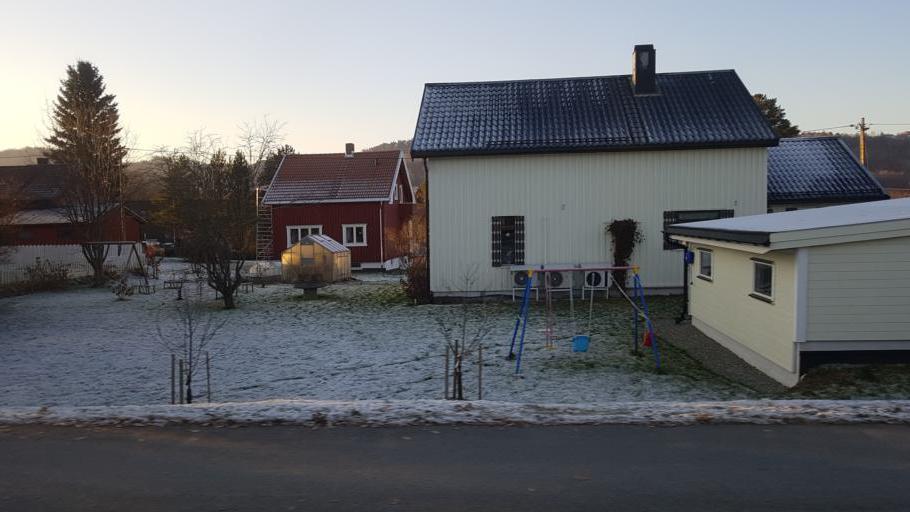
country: NO
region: Sor-Trondelag
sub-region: Melhus
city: Melhus
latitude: 63.3013
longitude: 10.2856
